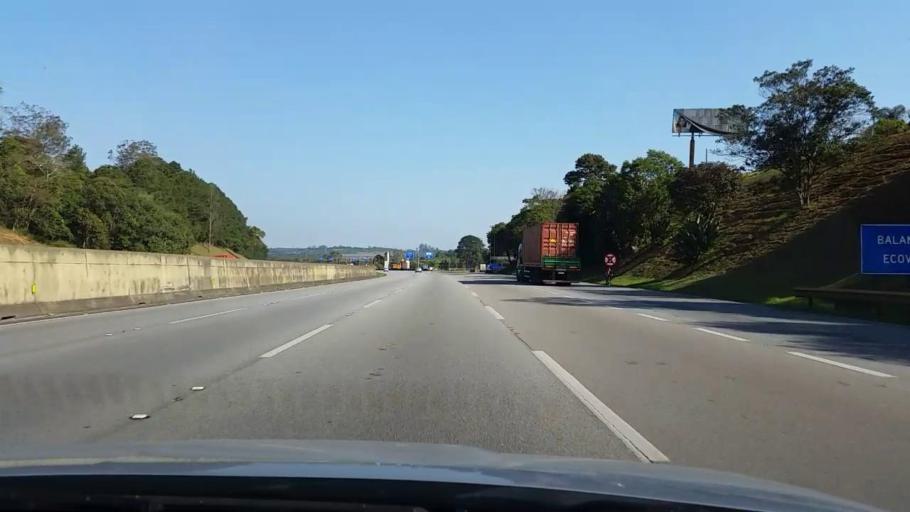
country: BR
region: Sao Paulo
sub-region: Sao Bernardo Do Campo
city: Sao Bernardo do Campo
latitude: -23.7787
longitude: -46.5967
